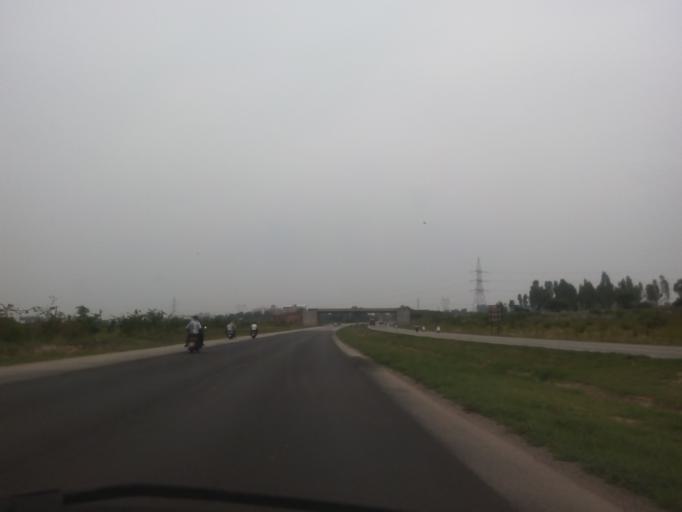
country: IN
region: Karnataka
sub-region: Bangalore Urban
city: Bangalore
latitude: 12.8669
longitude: 77.6360
